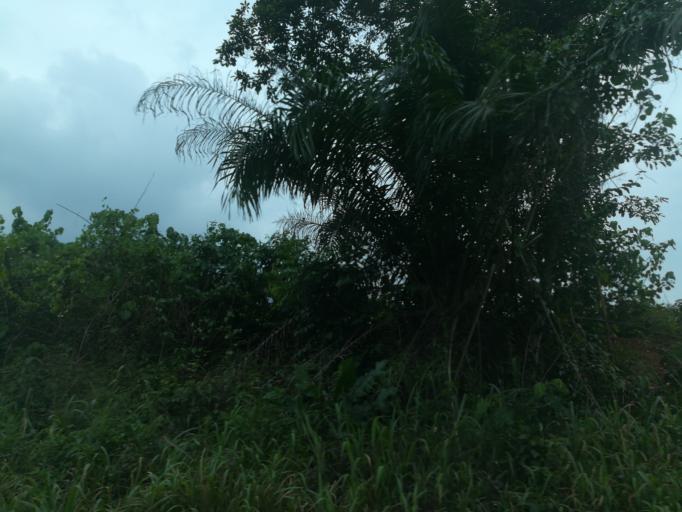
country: NG
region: Lagos
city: Ejirin
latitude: 6.6474
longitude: 3.7506
